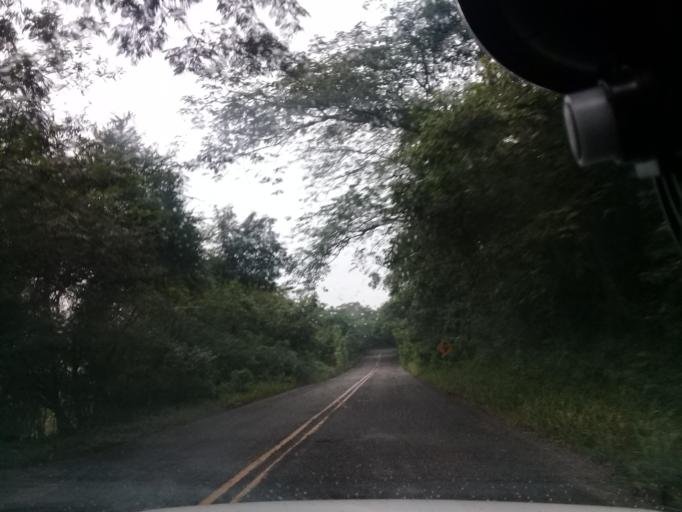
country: MX
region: Veracruz
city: Platon Sanchez
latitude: 21.2363
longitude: -98.3691
